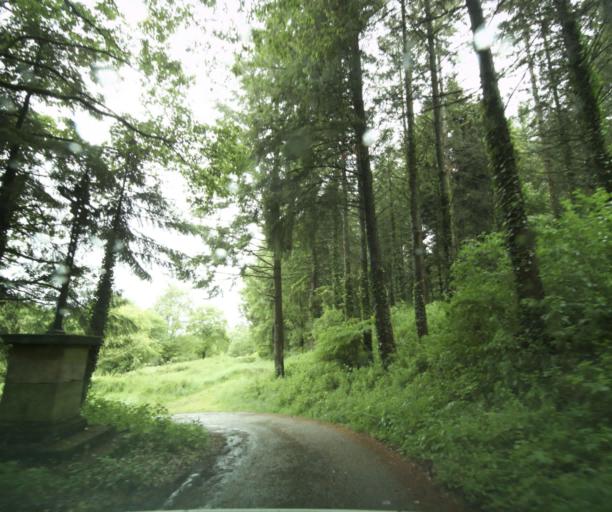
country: FR
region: Bourgogne
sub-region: Departement de Saone-et-Loire
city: Charolles
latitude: 46.5005
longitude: 4.3585
